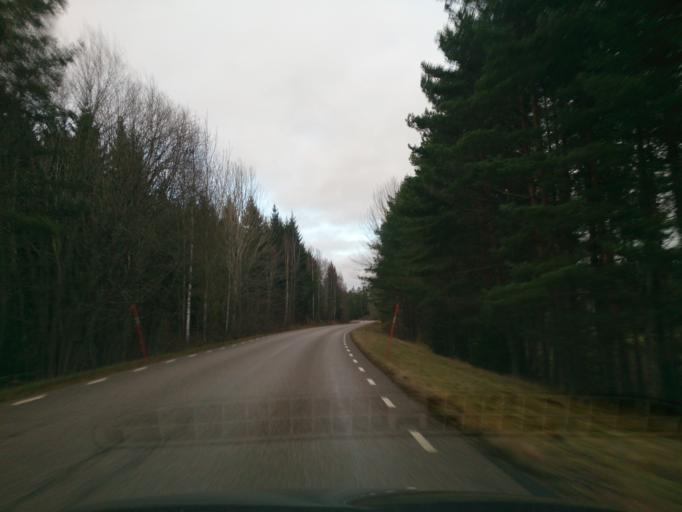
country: SE
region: OEstergoetland
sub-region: Atvidabergs Kommun
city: Atvidaberg
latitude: 58.2475
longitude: 16.0142
